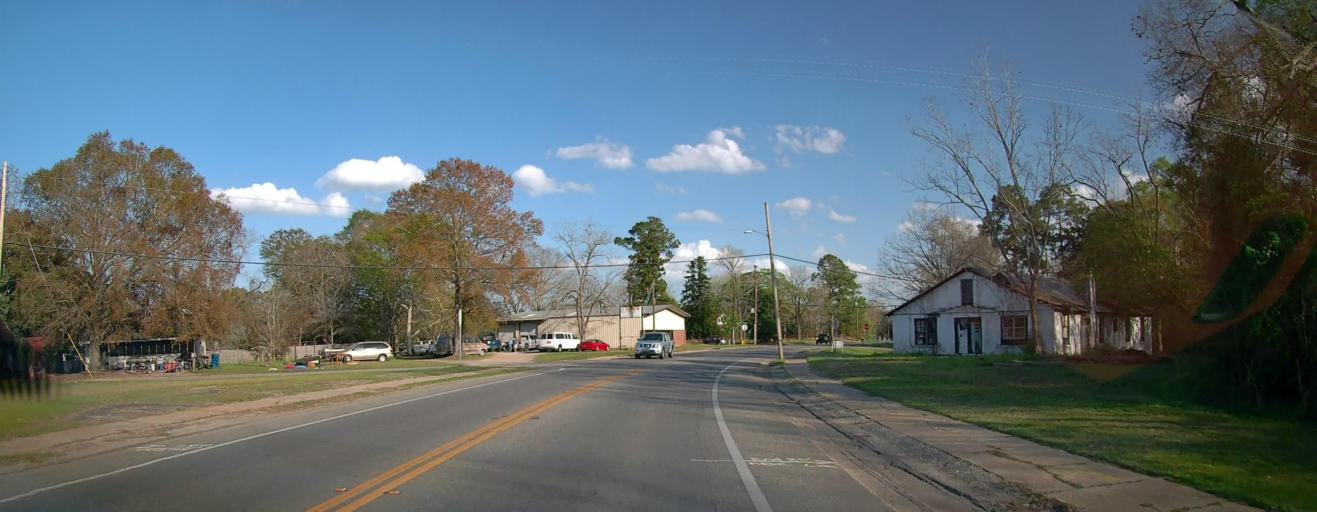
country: US
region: Georgia
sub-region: Toombs County
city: Lyons
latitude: 32.2029
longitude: -82.3191
